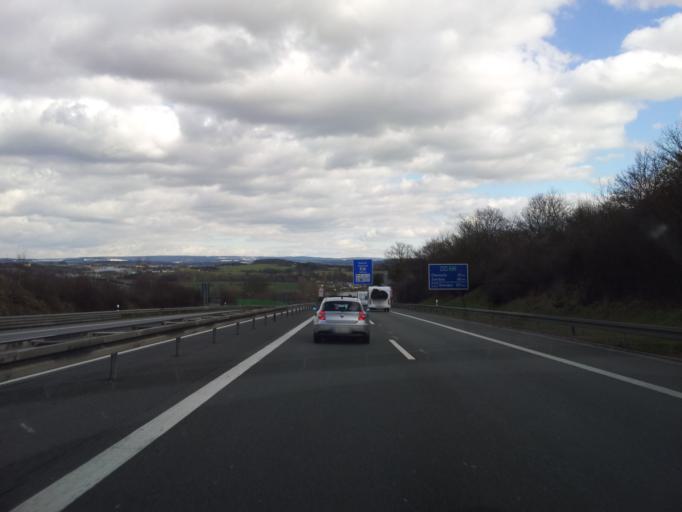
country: DE
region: Saxony
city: Weischlitz
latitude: 50.4346
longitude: 12.0980
